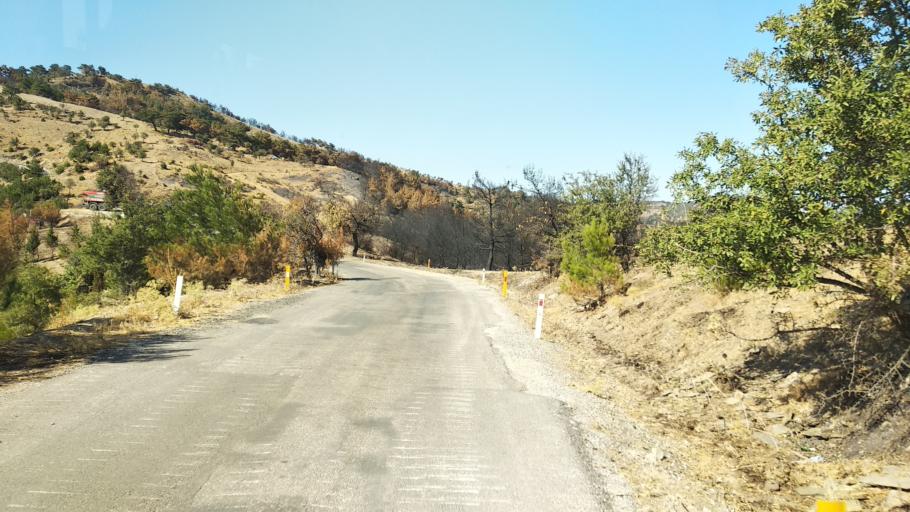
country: TR
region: Izmir
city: Gaziemir
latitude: 38.2926
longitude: 27.0013
